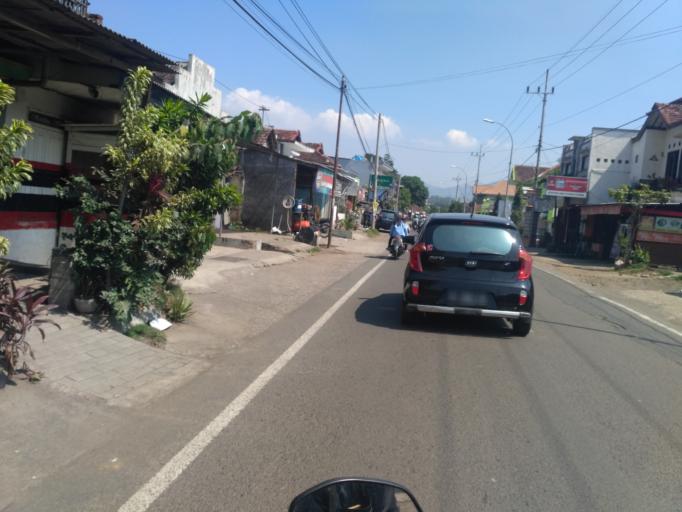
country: ID
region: East Java
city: Batu
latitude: -7.8640
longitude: 112.5568
